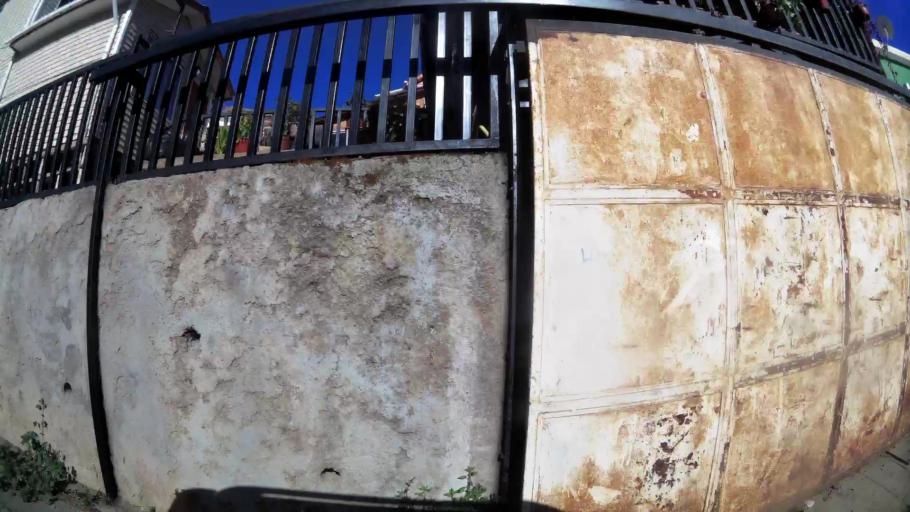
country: CL
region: Valparaiso
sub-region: Provincia de Valparaiso
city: Valparaiso
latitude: -33.0605
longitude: -71.6103
